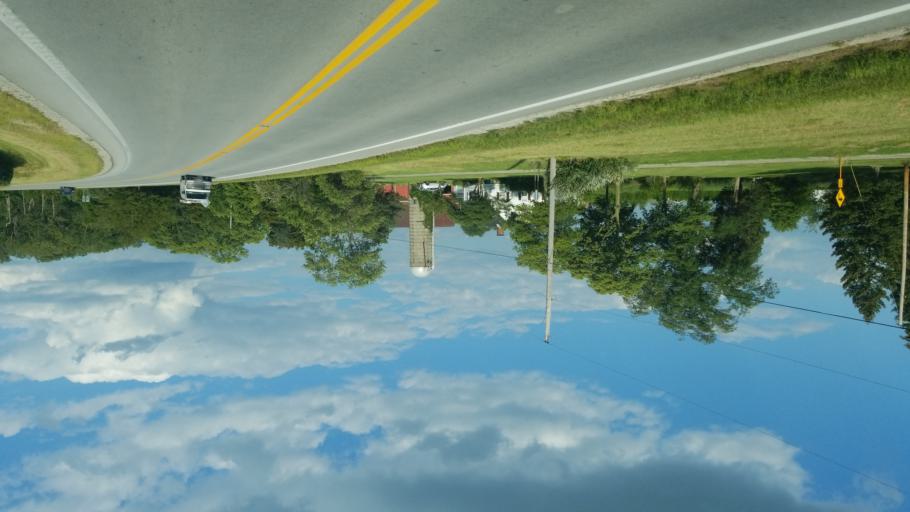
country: US
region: Ohio
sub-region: Wood County
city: Pemberville
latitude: 41.3622
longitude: -83.5124
